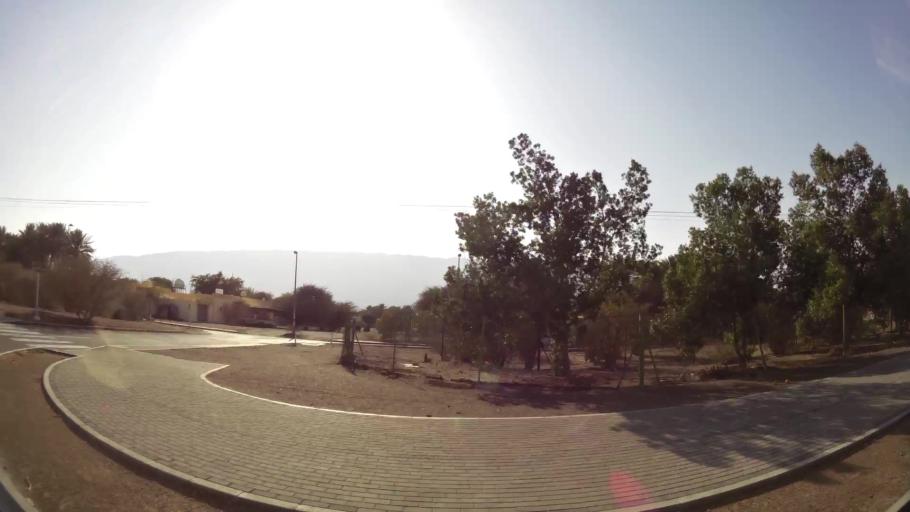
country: AE
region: Abu Dhabi
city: Al Ain
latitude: 24.0424
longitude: 55.8429
